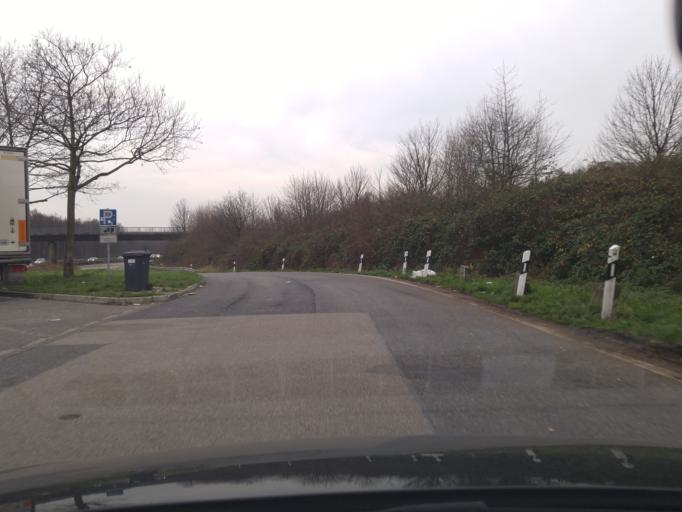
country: DE
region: North Rhine-Westphalia
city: Leichlingen
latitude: 51.0861
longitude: 6.9893
